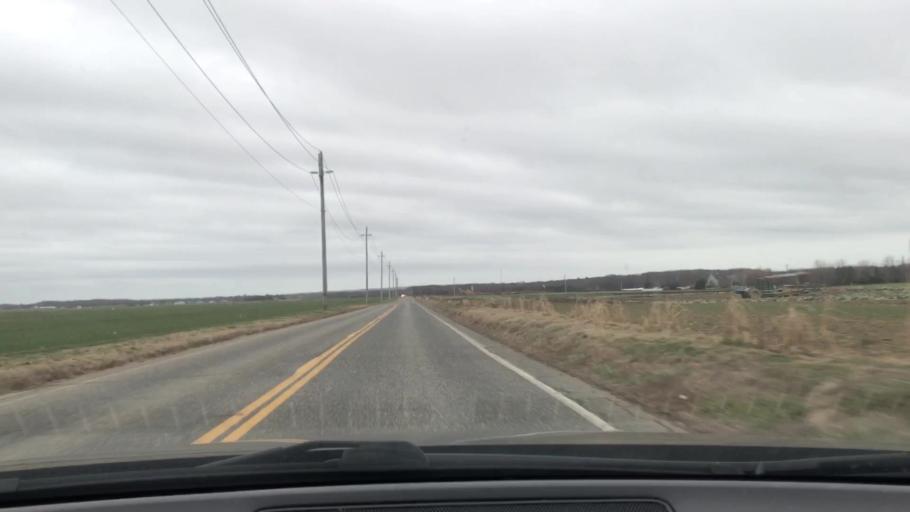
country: US
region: New York
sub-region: Suffolk County
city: Riverhead
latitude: 40.9651
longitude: -72.6734
